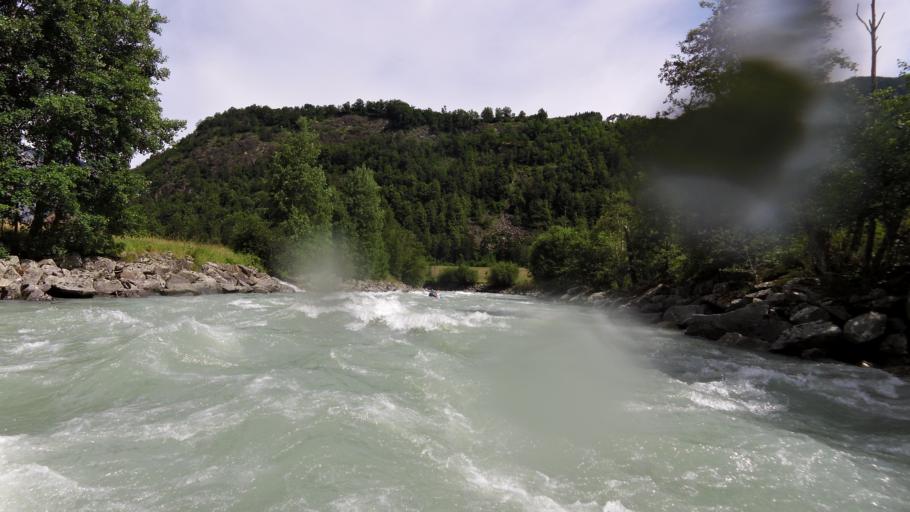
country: AT
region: Tyrol
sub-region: Politischer Bezirk Imst
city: Sautens
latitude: 47.2045
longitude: 10.8796
